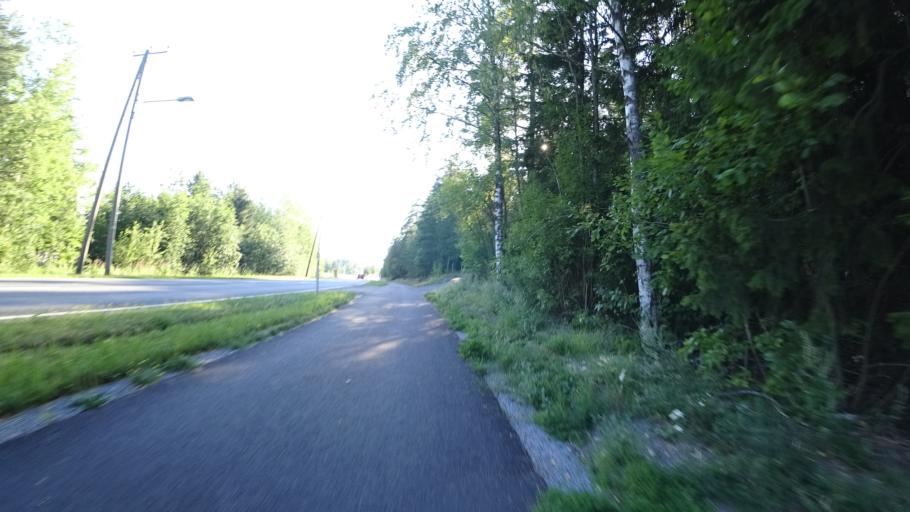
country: FI
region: Pirkanmaa
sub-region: Tampere
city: Pirkkala
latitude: 61.4846
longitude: 23.5694
